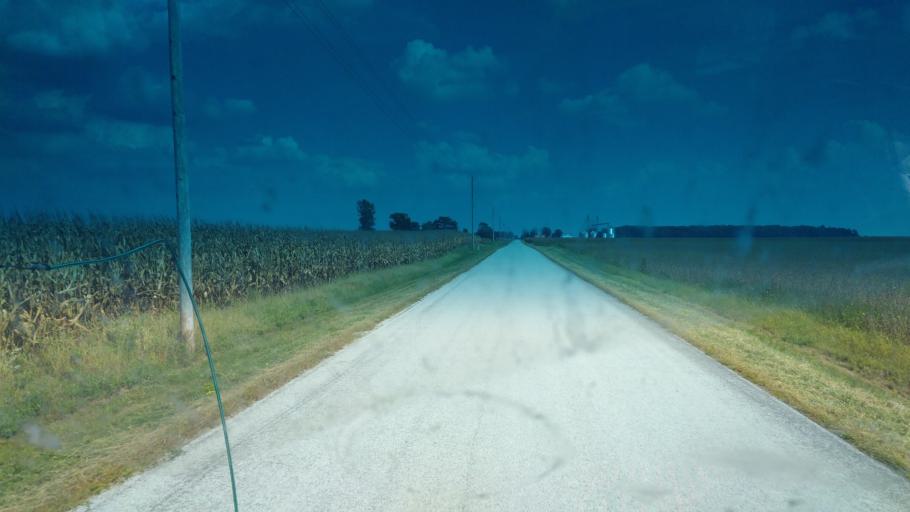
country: US
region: Ohio
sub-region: Hardin County
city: Kenton
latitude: 40.6589
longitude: -83.7218
